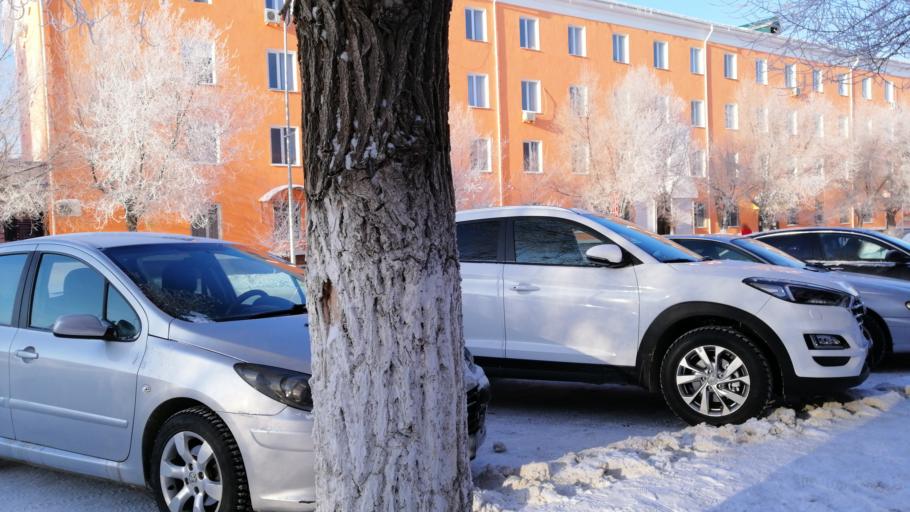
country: KZ
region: Aqtoebe
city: Aqtobe
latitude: 50.3105
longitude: 57.1473
